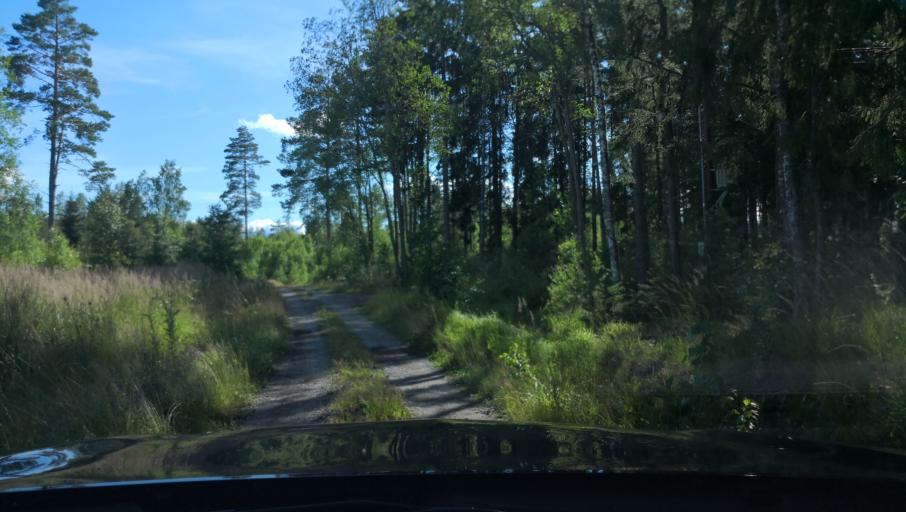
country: SE
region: Vaestmanland
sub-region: Surahammars Kommun
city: Surahammar
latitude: 59.6822
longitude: 16.2664
